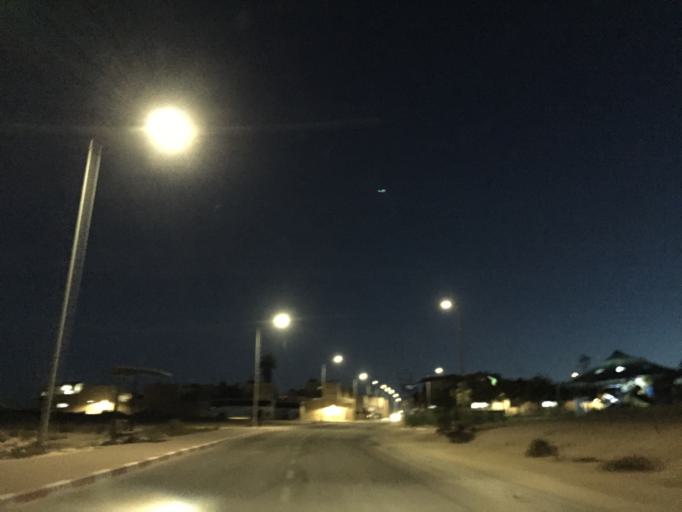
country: IL
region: Southern District
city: Mitzpe Ramon
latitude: 30.6143
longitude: 34.8004
